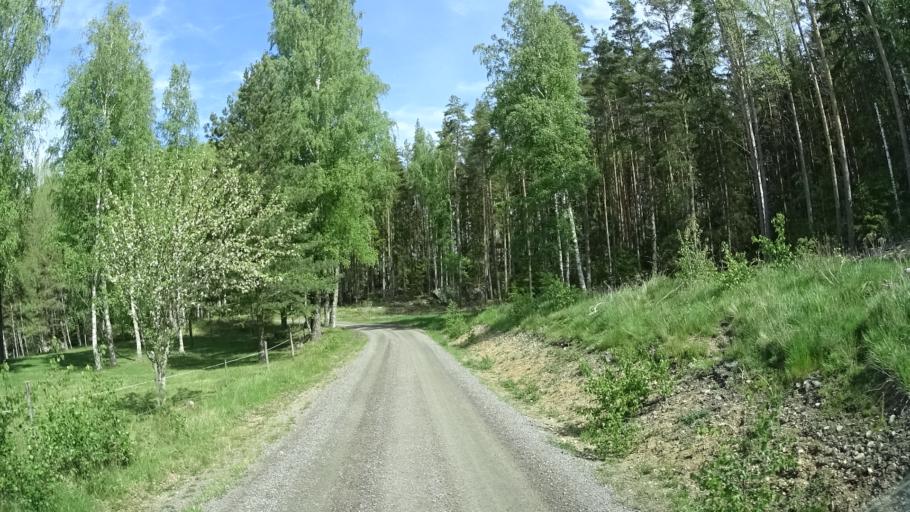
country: SE
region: OEstergoetland
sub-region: Finspangs Kommun
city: Finspang
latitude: 58.7888
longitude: 15.8719
